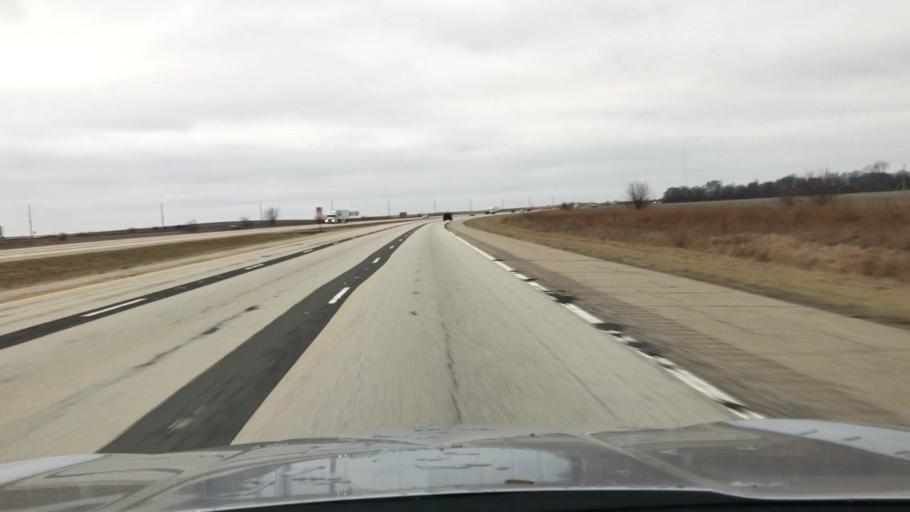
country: US
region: Illinois
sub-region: Sangamon County
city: Williamsville
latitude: 40.0079
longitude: -89.5007
